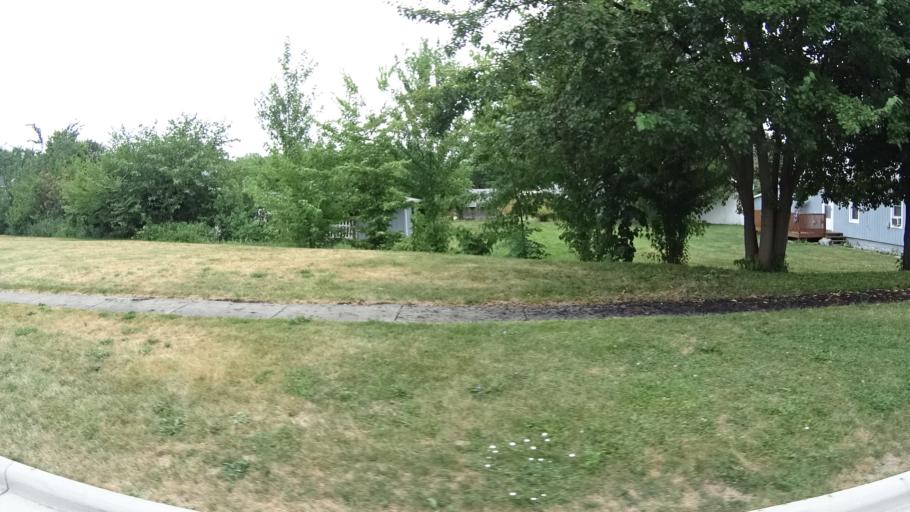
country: US
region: Ohio
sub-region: Erie County
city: Sandusky
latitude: 41.4490
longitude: -82.7018
